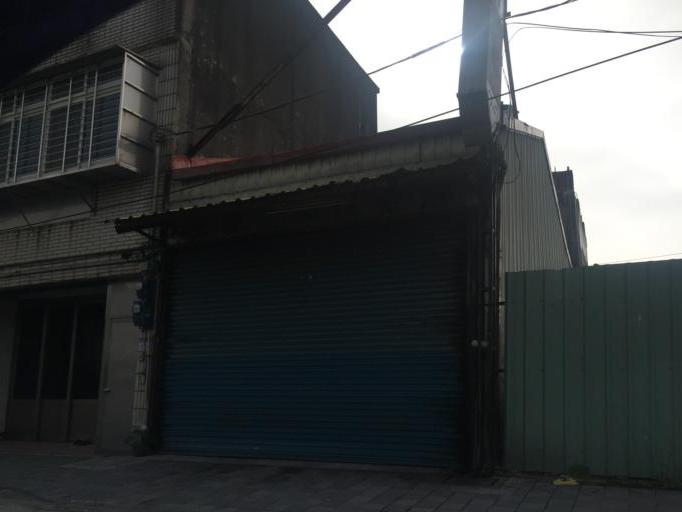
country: TW
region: Taiwan
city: Daxi
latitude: 24.8621
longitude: 121.2071
